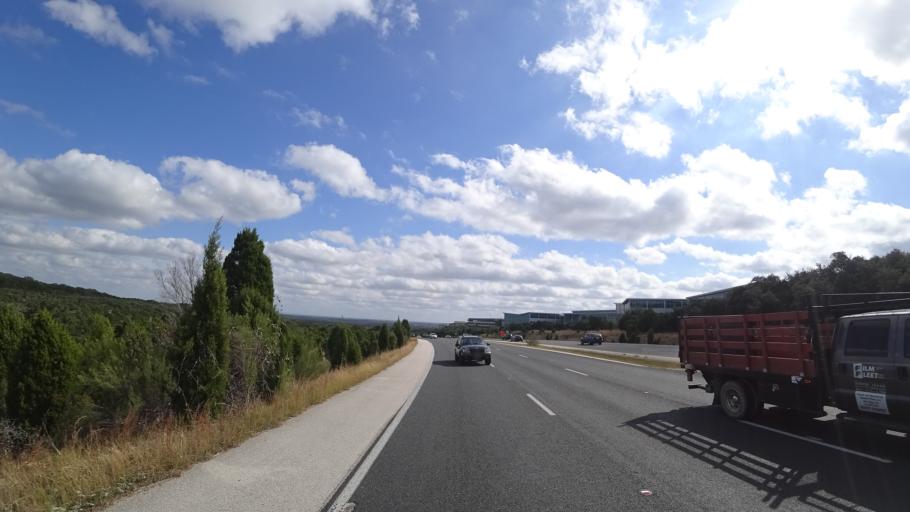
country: US
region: Texas
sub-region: Travis County
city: Barton Creek
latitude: 30.2528
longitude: -97.8632
